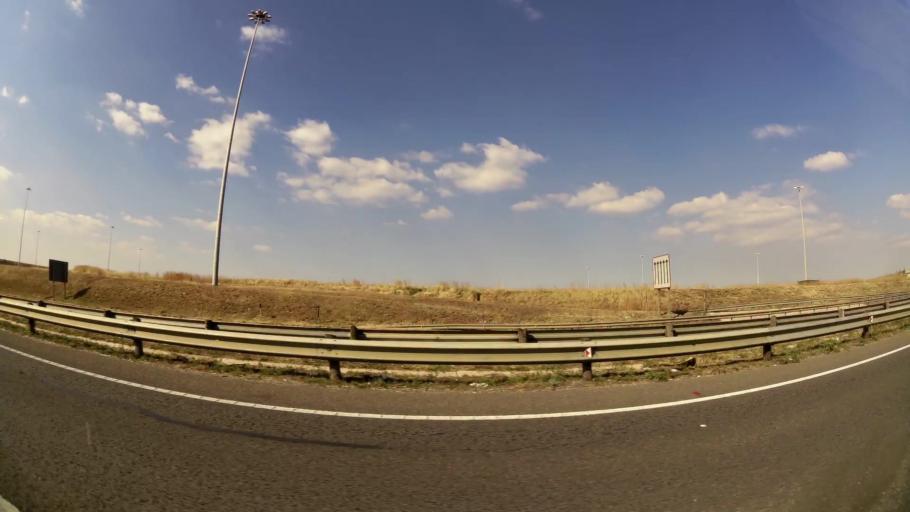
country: ZA
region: Gauteng
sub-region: City of Johannesburg Metropolitan Municipality
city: Modderfontein
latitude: -26.1022
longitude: 28.2512
